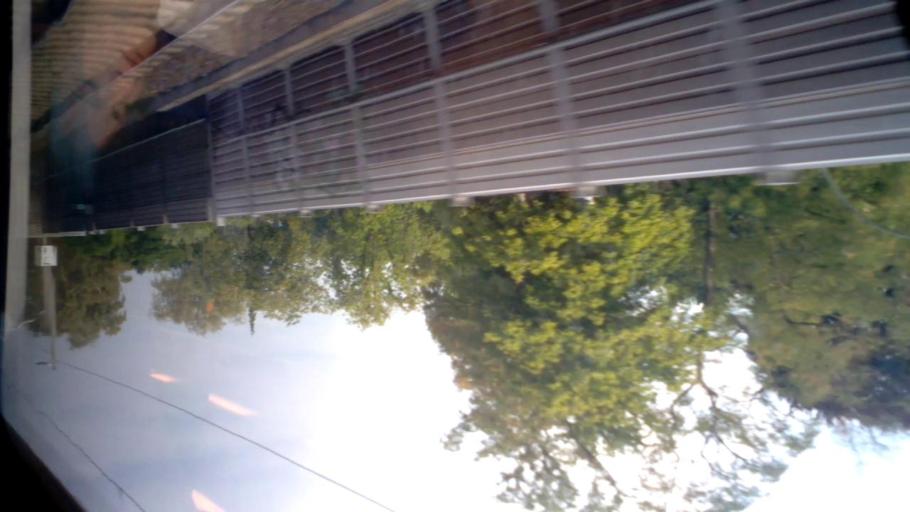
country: DE
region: Berlin
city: Lankwitz
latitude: 52.4394
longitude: 13.3433
